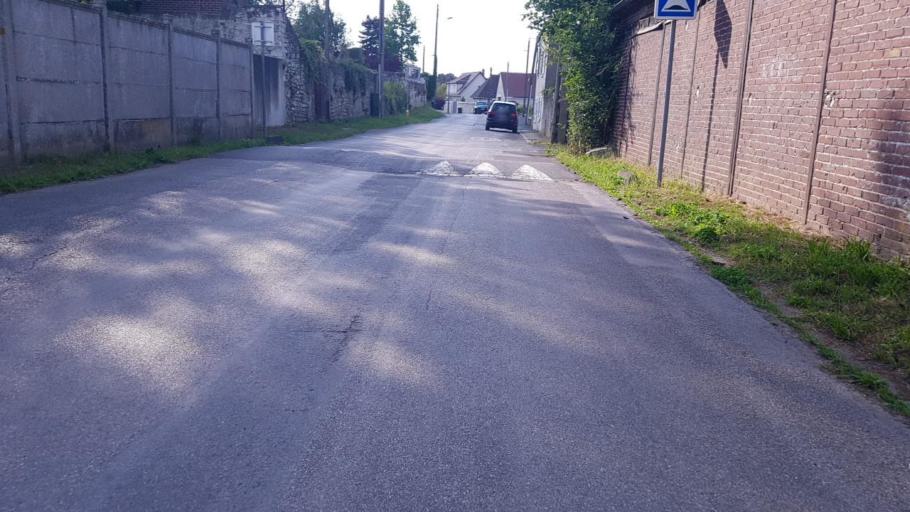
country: FR
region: Picardie
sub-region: Departement de l'Oise
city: Senlis
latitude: 49.1987
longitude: 2.5956
